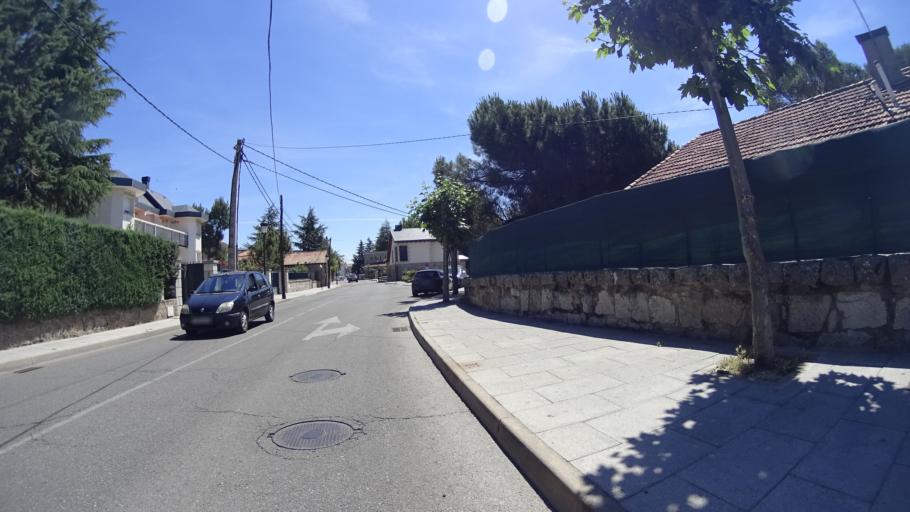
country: ES
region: Madrid
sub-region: Provincia de Madrid
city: Hoyo de Manzanares
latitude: 40.6218
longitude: -3.9106
